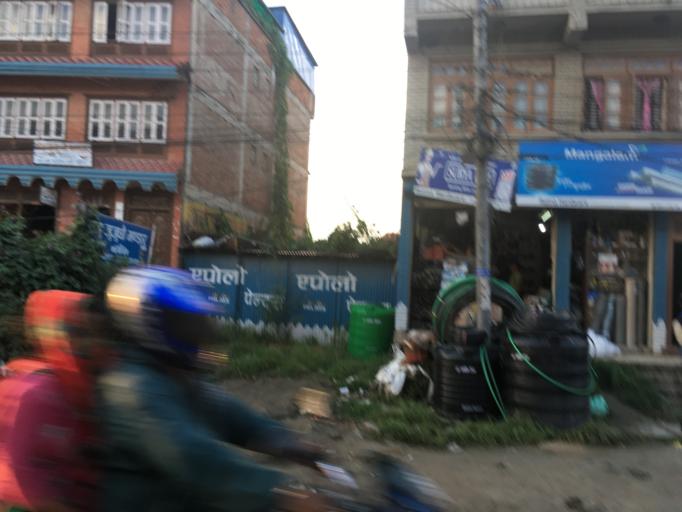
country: NP
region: Central Region
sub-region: Bagmati Zone
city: Bhaktapur
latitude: 27.6786
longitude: 85.4413
